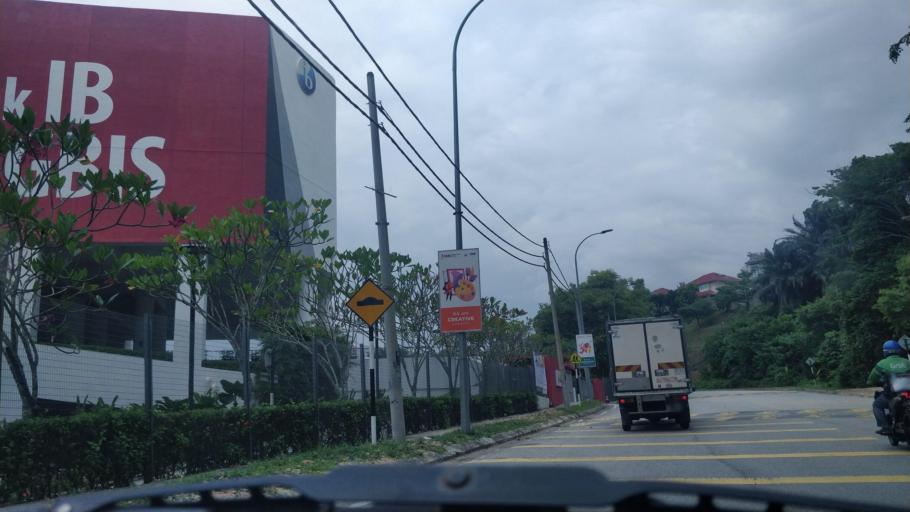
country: MY
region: Selangor
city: Kuang
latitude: 3.2041
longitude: 101.5880
